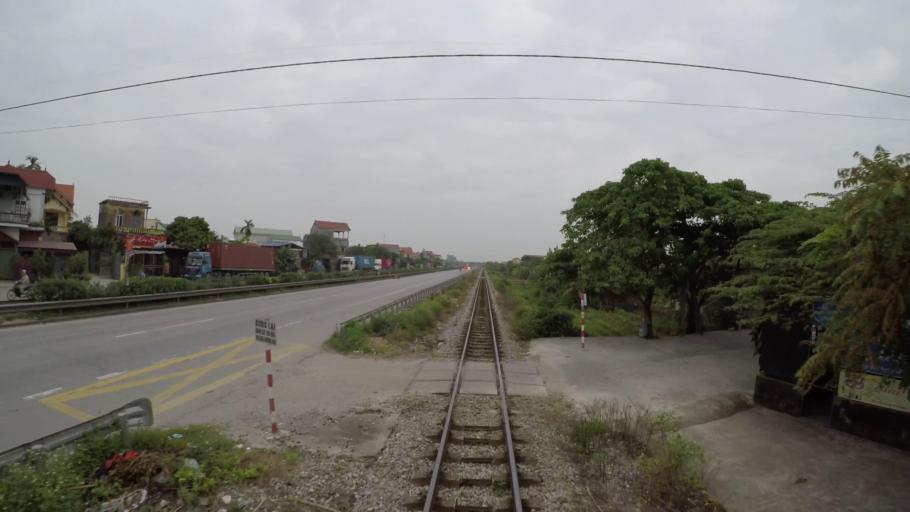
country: VN
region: Hai Duong
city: Phu Thai
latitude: 20.9584
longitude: 106.5239
